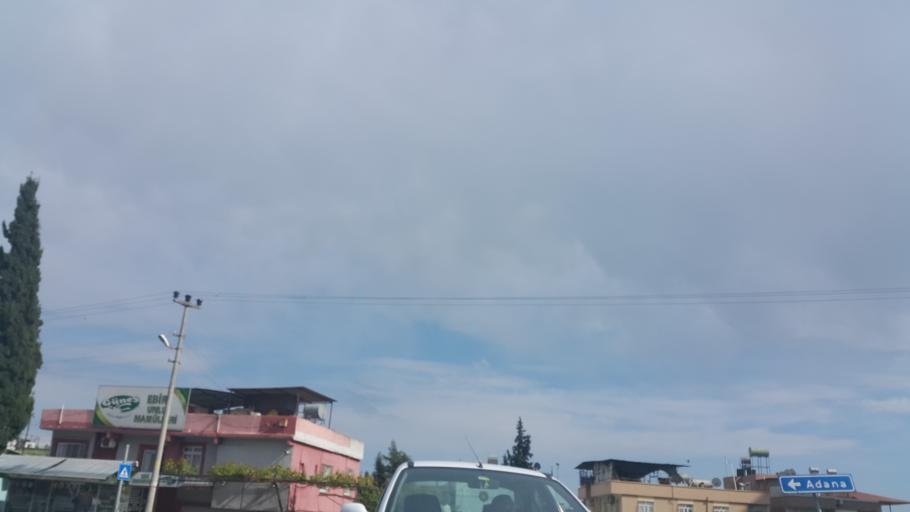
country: TR
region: Mersin
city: Tarsus
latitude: 36.9074
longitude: 34.8858
